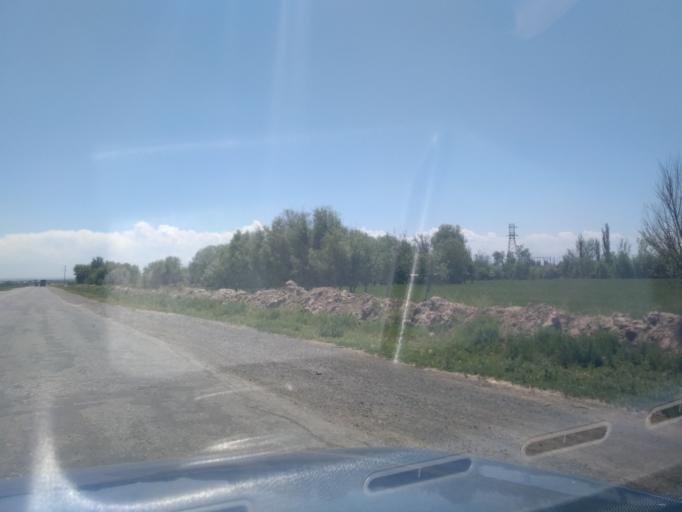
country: UZ
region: Sirdaryo
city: Yangiyer
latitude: 40.2317
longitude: 68.8474
